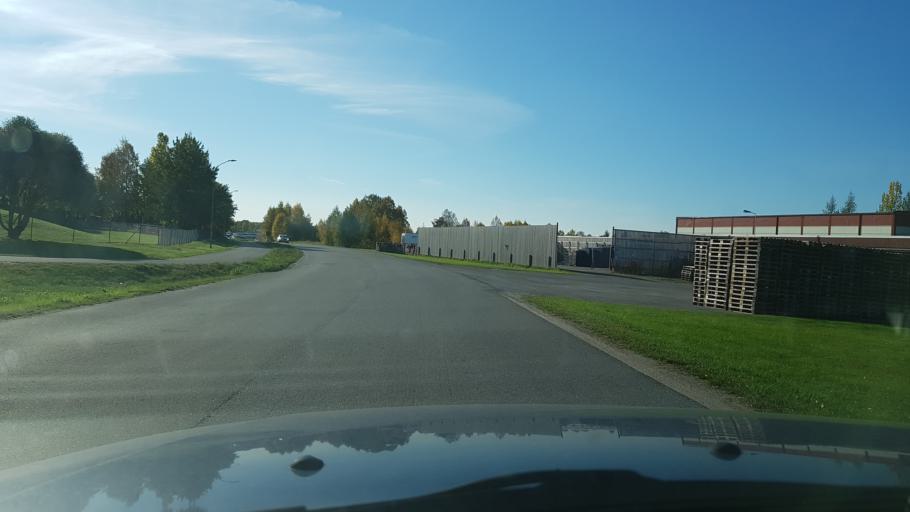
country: SE
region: Norrbotten
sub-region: Pitea Kommun
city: Bergsviken
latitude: 65.3454
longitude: 21.4092
